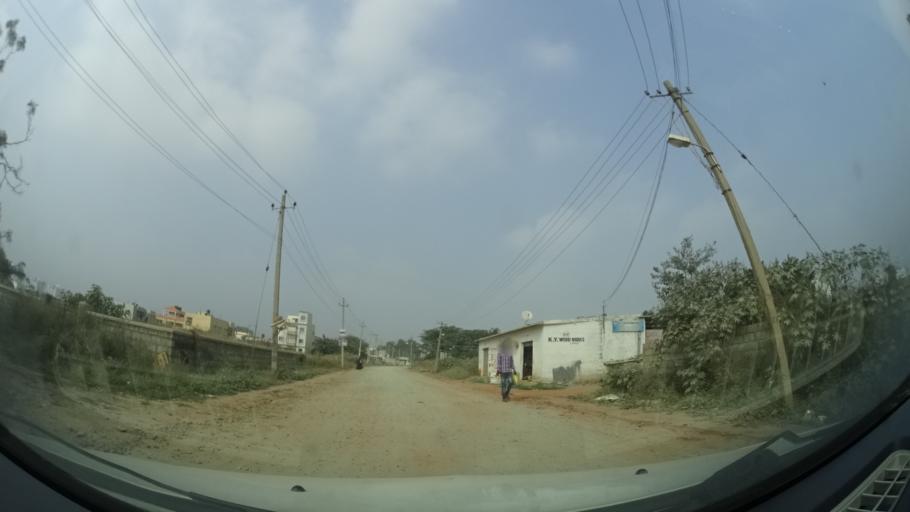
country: IN
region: Karnataka
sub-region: Bangalore Urban
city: Anekal
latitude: 12.8319
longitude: 77.6614
